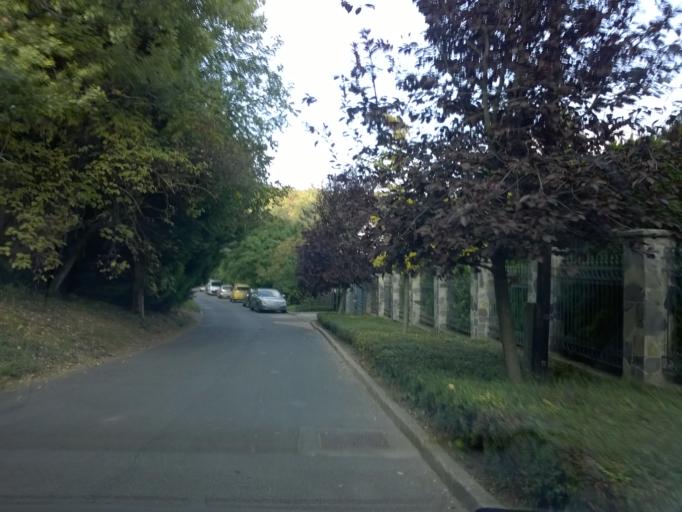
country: HU
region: Budapest
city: Budapest II. keruelet
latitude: 47.5359
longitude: 19.0124
